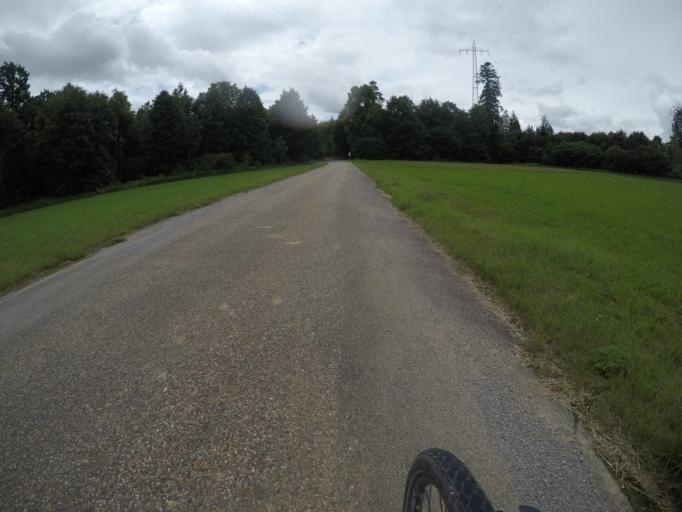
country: DE
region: Baden-Wuerttemberg
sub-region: Regierungsbezirk Stuttgart
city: Oberjettingen
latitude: 48.5973
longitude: 8.8077
